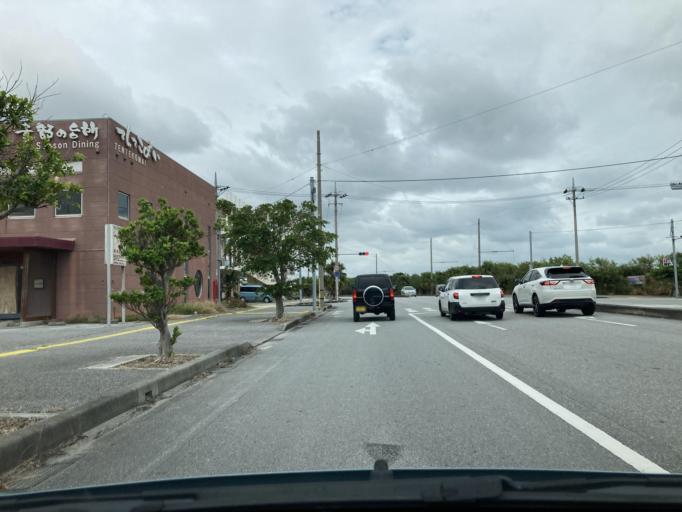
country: JP
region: Okinawa
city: Ginowan
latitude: 26.2089
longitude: 127.7639
